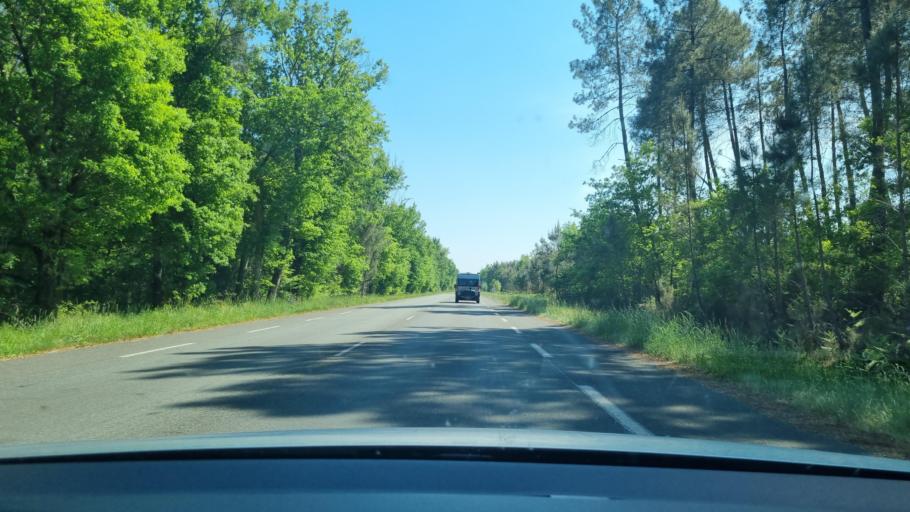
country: FR
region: Aquitaine
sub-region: Departement de la Gironde
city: Prechac
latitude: 44.2512
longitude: -0.2612
